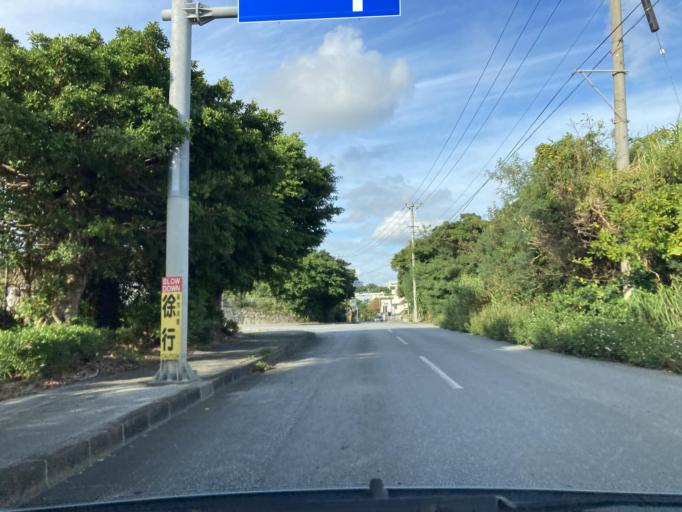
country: JP
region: Okinawa
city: Itoman
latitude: 26.1397
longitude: 127.7472
